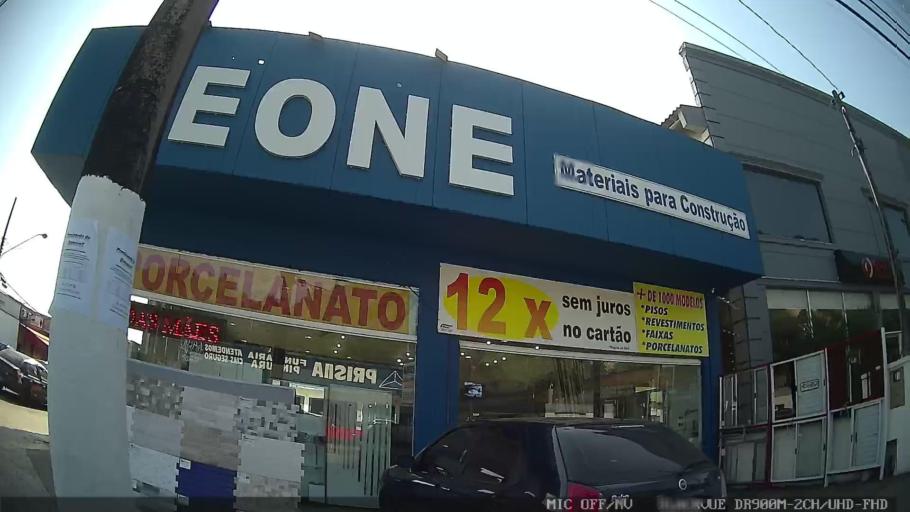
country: BR
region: Sao Paulo
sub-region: Guaruja
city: Guaruja
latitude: -23.9918
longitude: -46.2706
